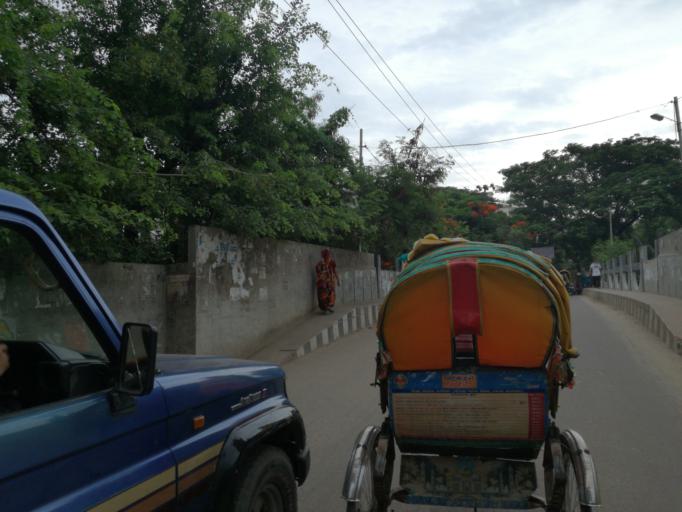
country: BD
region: Dhaka
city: Paltan
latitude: 23.7745
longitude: 90.4136
